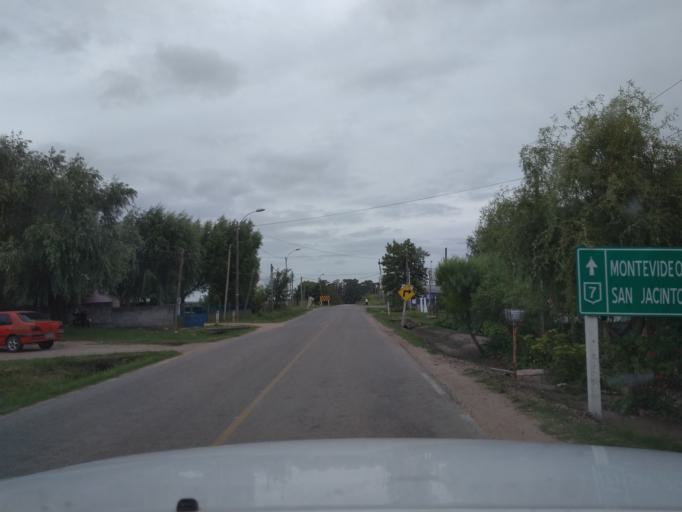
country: UY
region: Canelones
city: Tala
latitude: -34.3472
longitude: -55.7599
